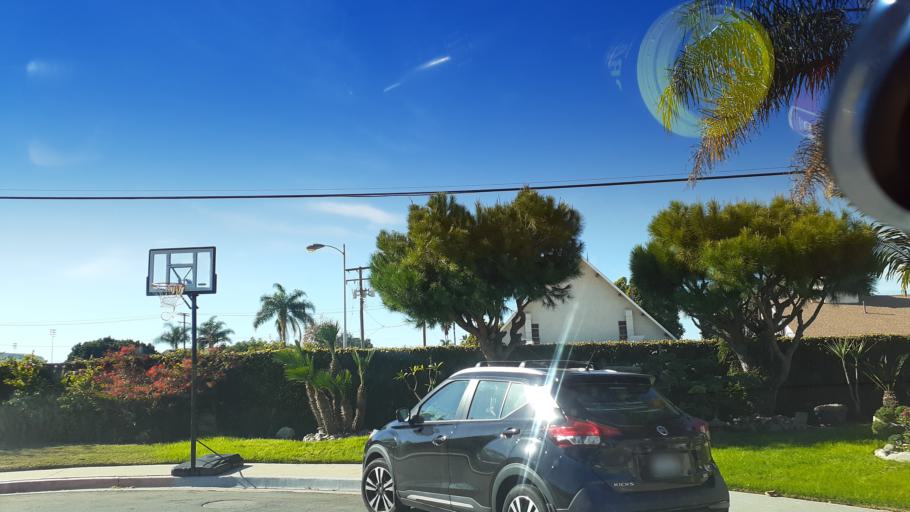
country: US
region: California
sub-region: Los Angeles County
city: Artesia
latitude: 33.8612
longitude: -118.0744
